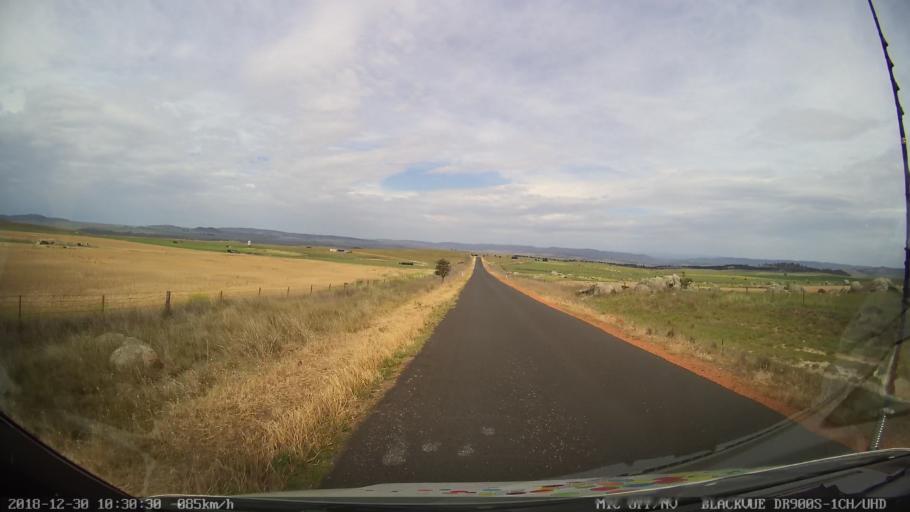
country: AU
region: New South Wales
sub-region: Snowy River
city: Berridale
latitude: -36.5039
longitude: 148.8942
